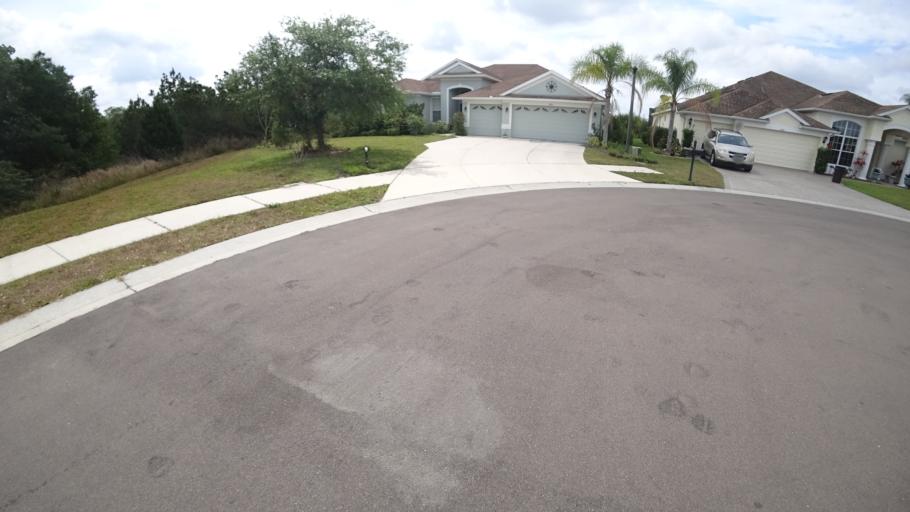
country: US
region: Florida
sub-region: Manatee County
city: Ellenton
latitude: 27.5322
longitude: -82.4110
